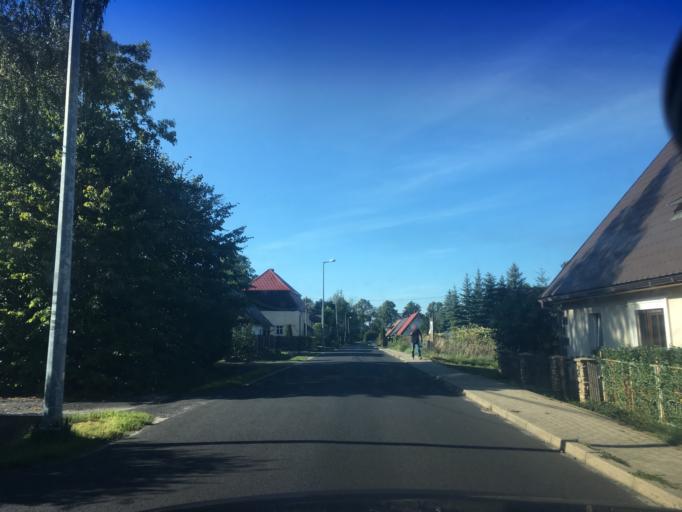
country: PL
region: Lower Silesian Voivodeship
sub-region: Powiat lubanski
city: Swieradow-Zdroj
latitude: 50.9320
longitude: 15.3031
